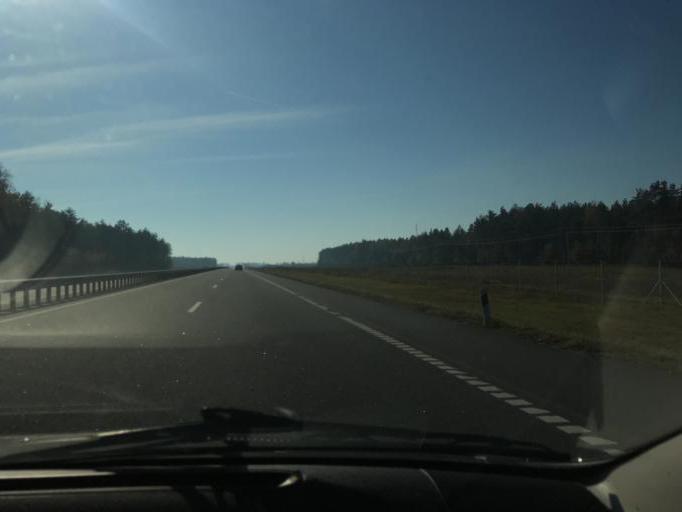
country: BY
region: Minsk
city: Slutsk
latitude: 53.2412
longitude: 27.5502
